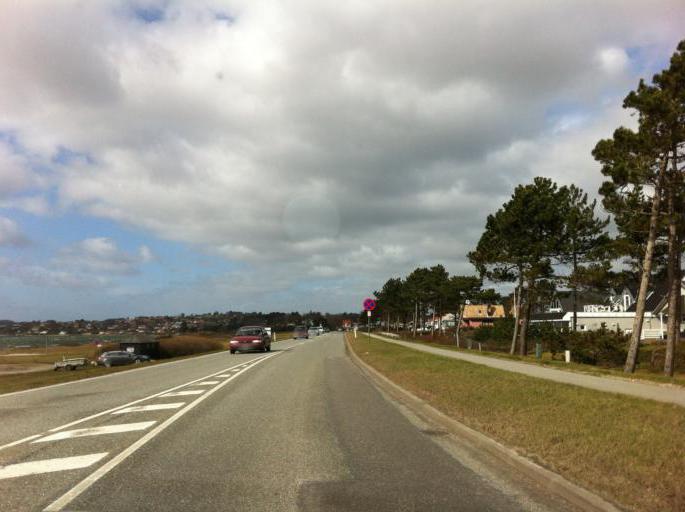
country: DK
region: Central Jutland
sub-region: Syddjurs Kommune
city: Ebeltoft
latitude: 56.2183
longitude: 10.6714
